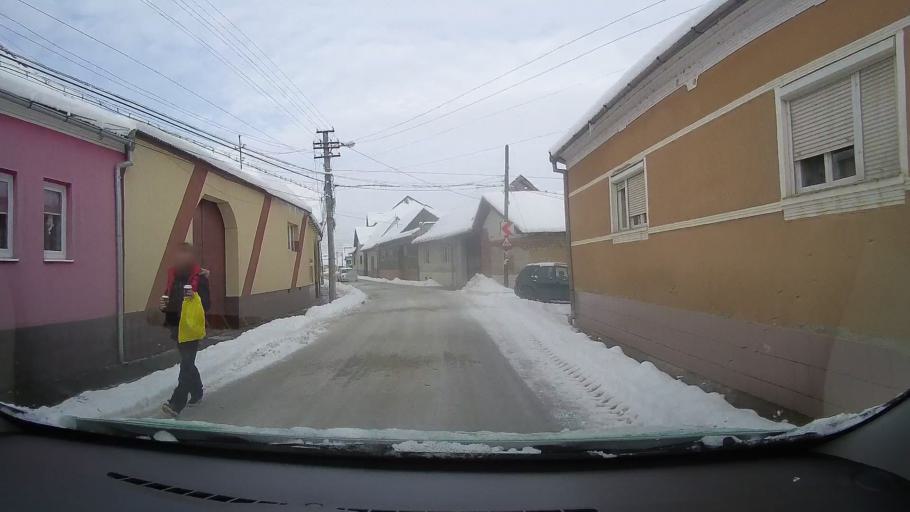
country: RO
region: Alba
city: Pianu de Sus
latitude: 45.8945
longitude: 23.4833
